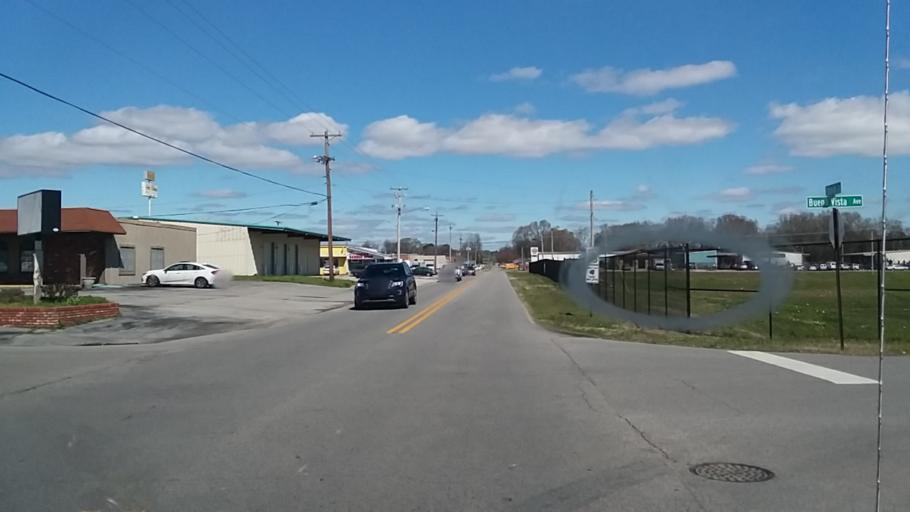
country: US
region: Alabama
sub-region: Colbert County
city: Muscle Shoals
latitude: 34.7455
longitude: -87.6654
